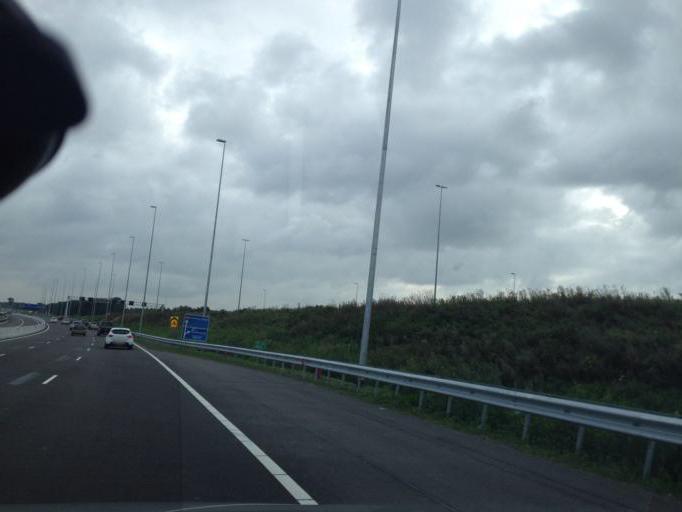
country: NL
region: North Holland
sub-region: Gemeente Naarden
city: Naarden
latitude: 52.3156
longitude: 5.1143
